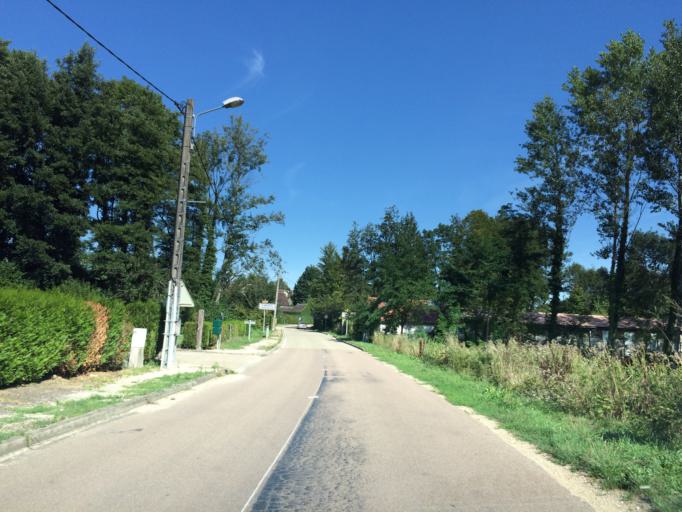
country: FR
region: Bourgogne
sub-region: Departement de l'Yonne
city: Aillant-sur-Tholon
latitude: 47.8312
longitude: 3.3616
